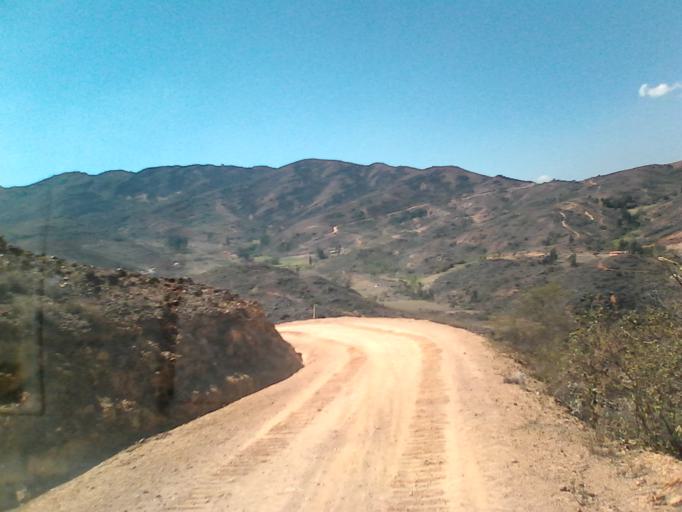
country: CO
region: Boyaca
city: Sachica
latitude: 5.5524
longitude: -73.5656
